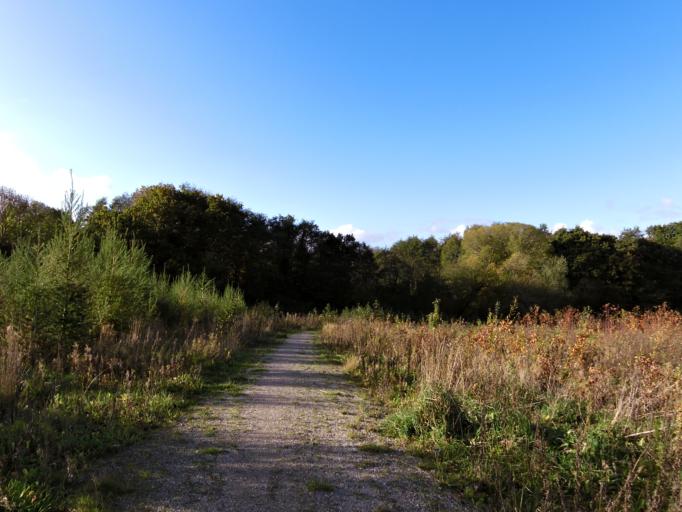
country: DK
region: Central Jutland
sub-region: Arhus Kommune
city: Framlev
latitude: 56.1234
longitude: 10.0265
